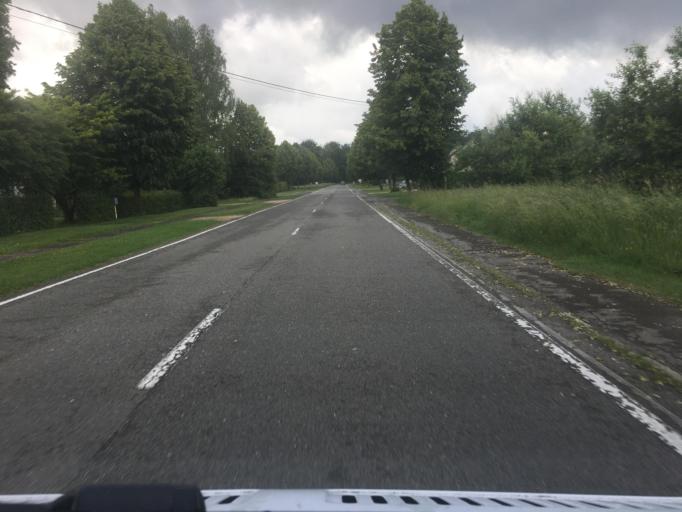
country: BE
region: Wallonia
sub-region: Province du Luxembourg
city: Florenville
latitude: 49.6841
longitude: 5.3309
